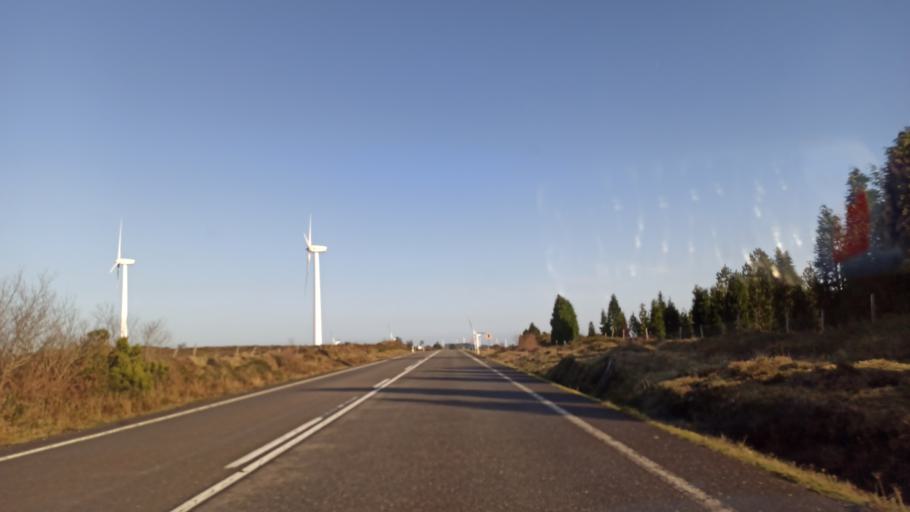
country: ES
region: Galicia
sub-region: Provincia da Coruna
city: As Pontes de Garcia Rodriguez
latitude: 43.5430
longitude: -7.8045
